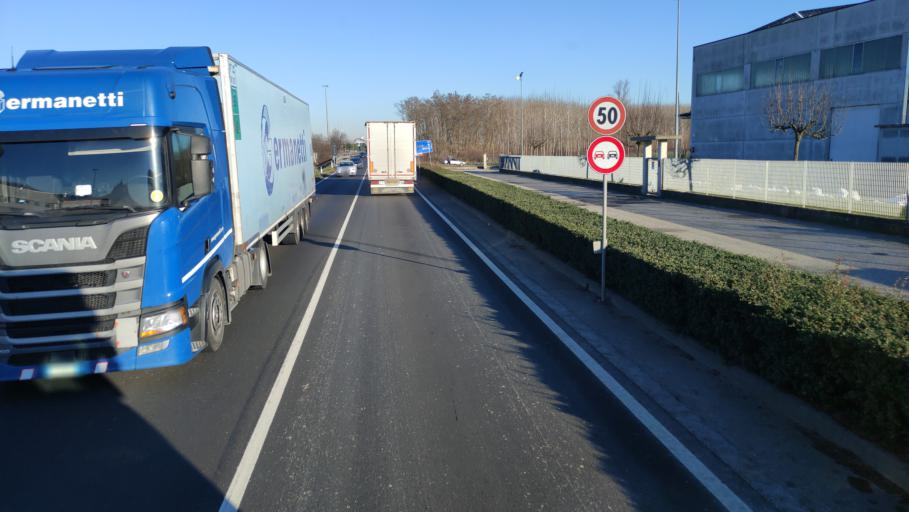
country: IT
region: Piedmont
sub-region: Provincia di Cuneo
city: Borgo
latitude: 44.6977
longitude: 7.9561
